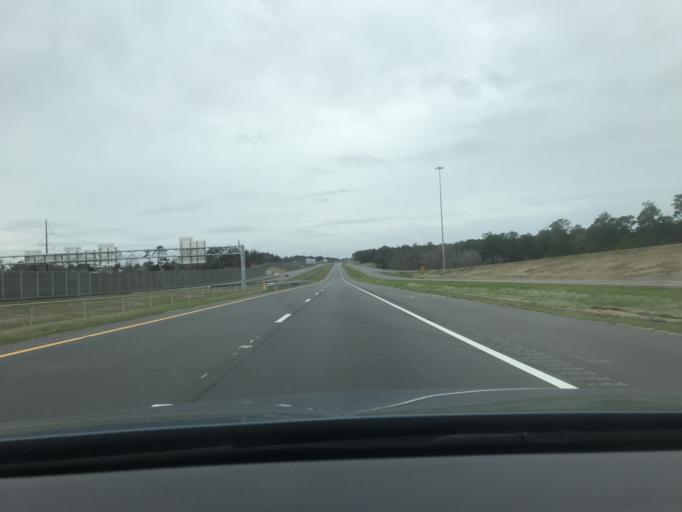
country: US
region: North Carolina
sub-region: Cumberland County
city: Fort Bragg
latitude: 35.1110
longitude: -78.9779
